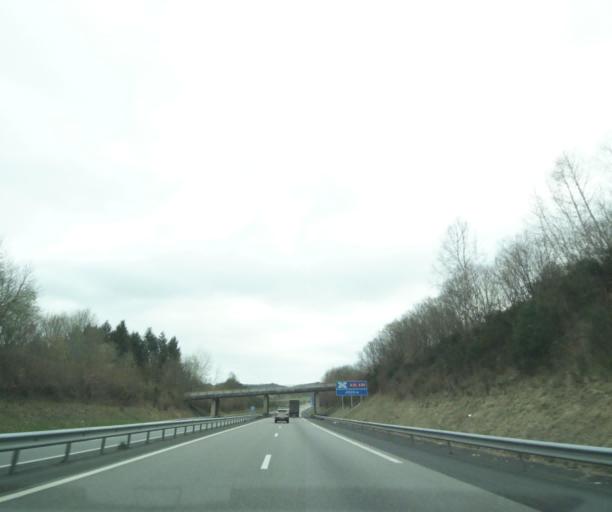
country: FR
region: Limousin
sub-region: Departement de la Correze
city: Vigeois
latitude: 45.3437
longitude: 1.5713
